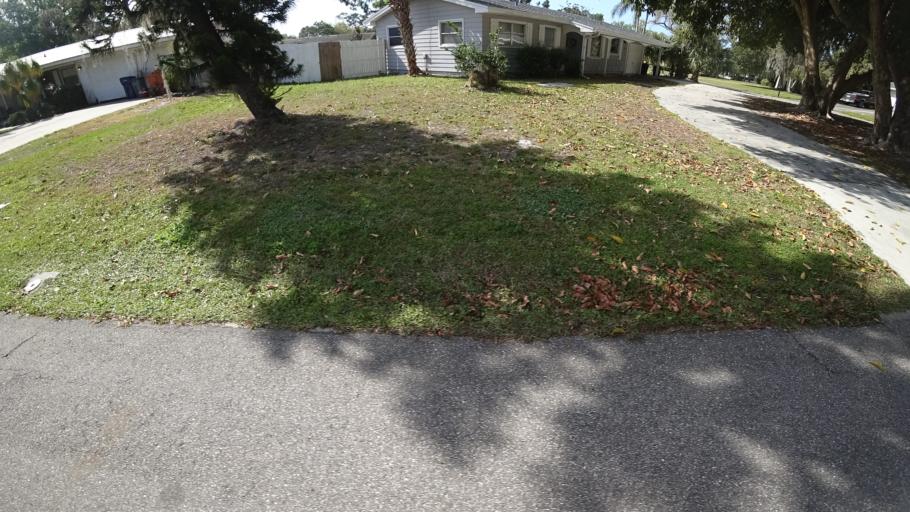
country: US
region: Florida
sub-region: Manatee County
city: Whitfield
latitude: 27.4227
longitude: -82.5584
